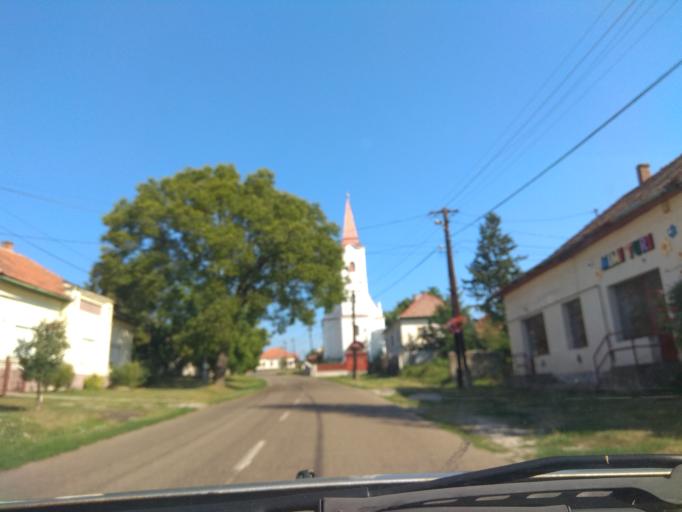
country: HU
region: Borsod-Abauj-Zemplen
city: Emod
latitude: 47.9437
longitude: 20.8139
